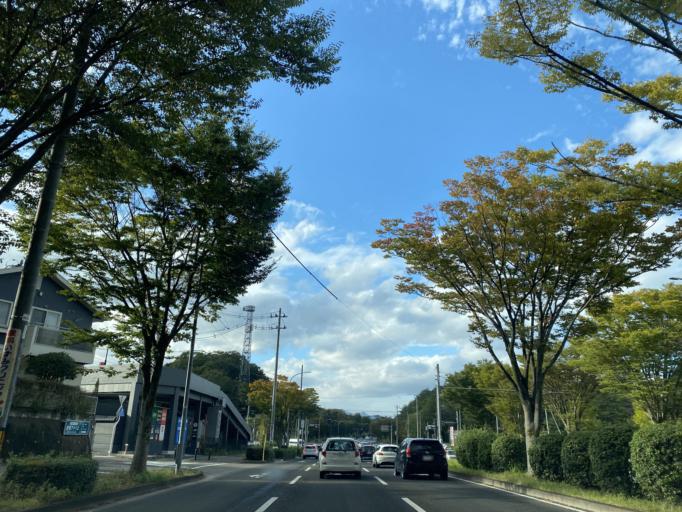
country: JP
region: Miyagi
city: Sendai-shi
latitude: 38.3097
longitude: 140.8485
